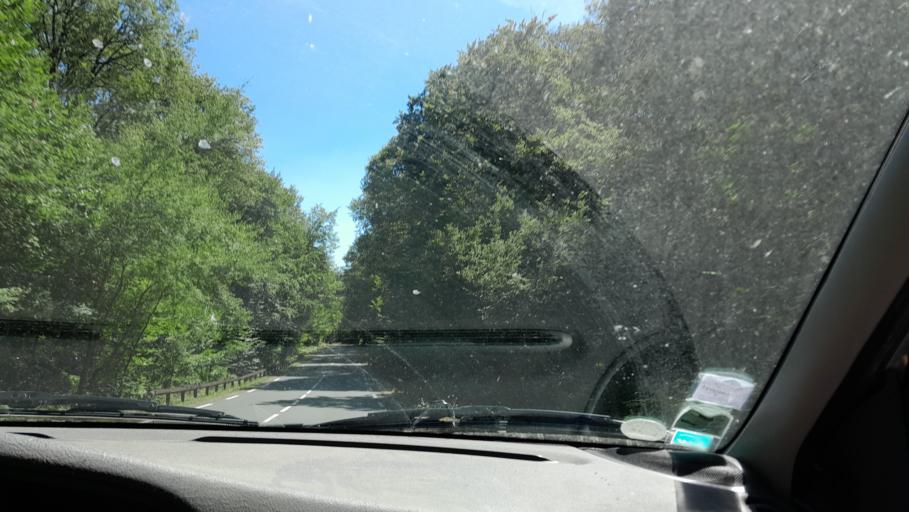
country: FR
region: Pays de la Loire
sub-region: Departement de Maine-et-Loire
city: Pouance
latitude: 47.6905
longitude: -1.1851
